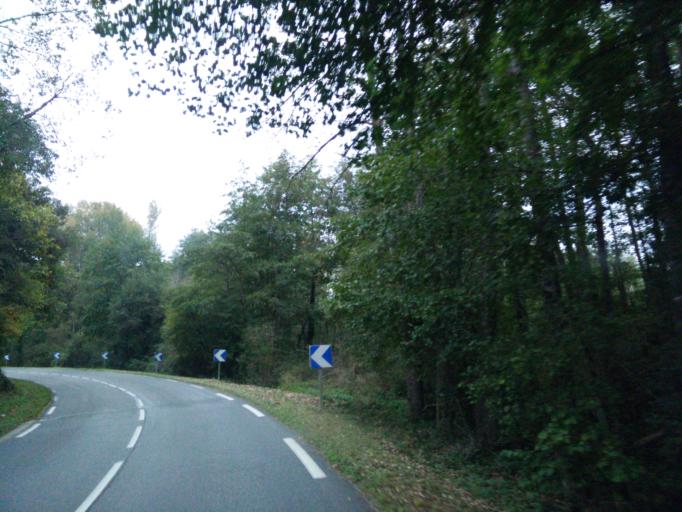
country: FR
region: Aquitaine
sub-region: Departement de la Dordogne
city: Carsac-Aillac
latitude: 44.7982
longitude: 1.3008
